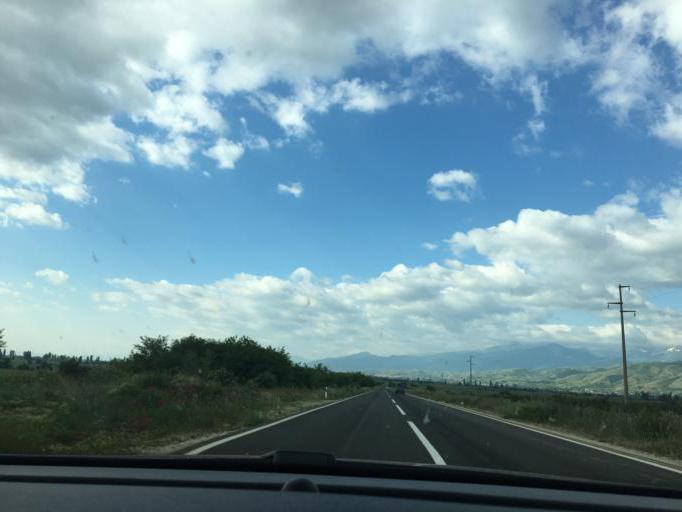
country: MK
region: Mogila
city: Beranci
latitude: 41.1326
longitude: 21.3628
